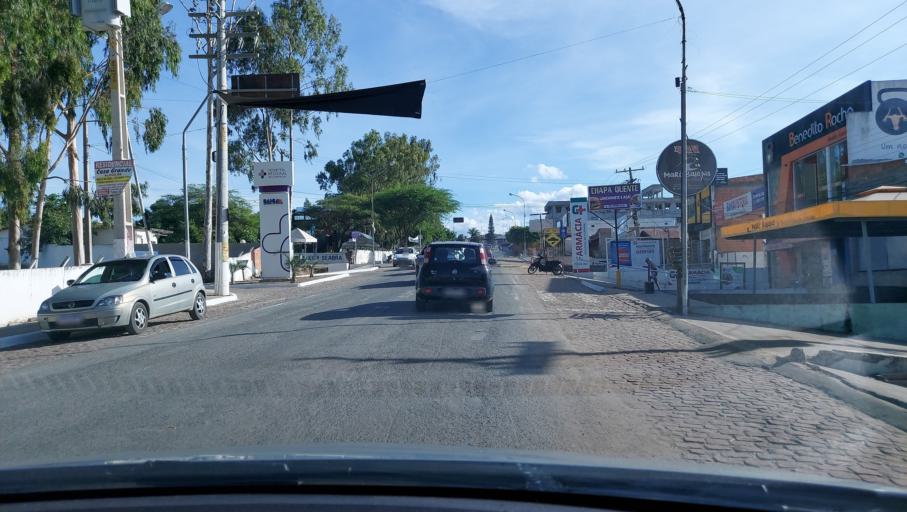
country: BR
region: Bahia
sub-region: Seabra
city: Seabra
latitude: -12.4252
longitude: -41.7693
